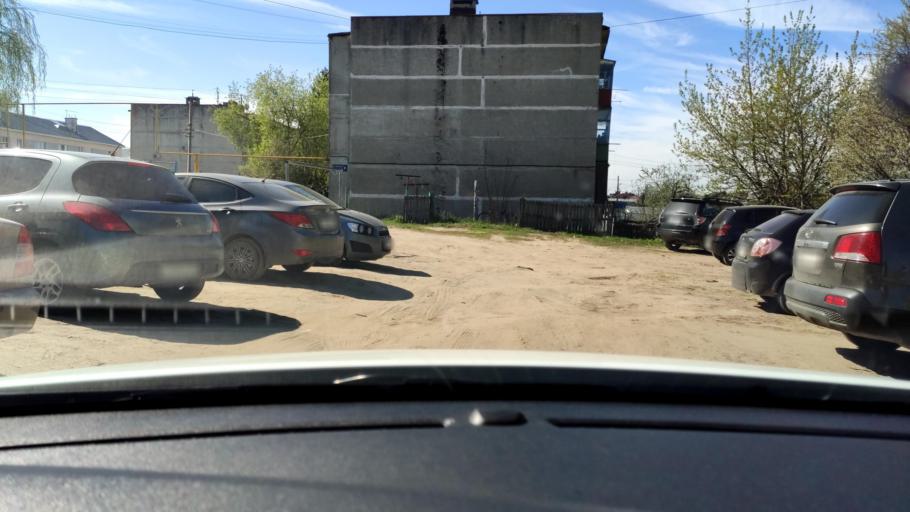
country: RU
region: Tatarstan
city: Vysokaya Gora
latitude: 55.8767
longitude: 49.2470
